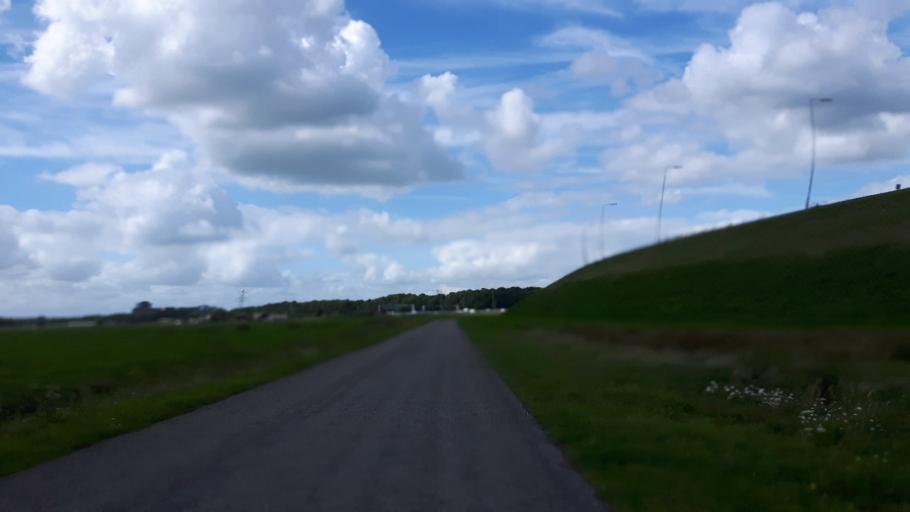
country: NL
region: Utrecht
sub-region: Gemeente Nieuwegein
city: Nieuwegein
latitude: 52.0631
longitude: 5.0658
